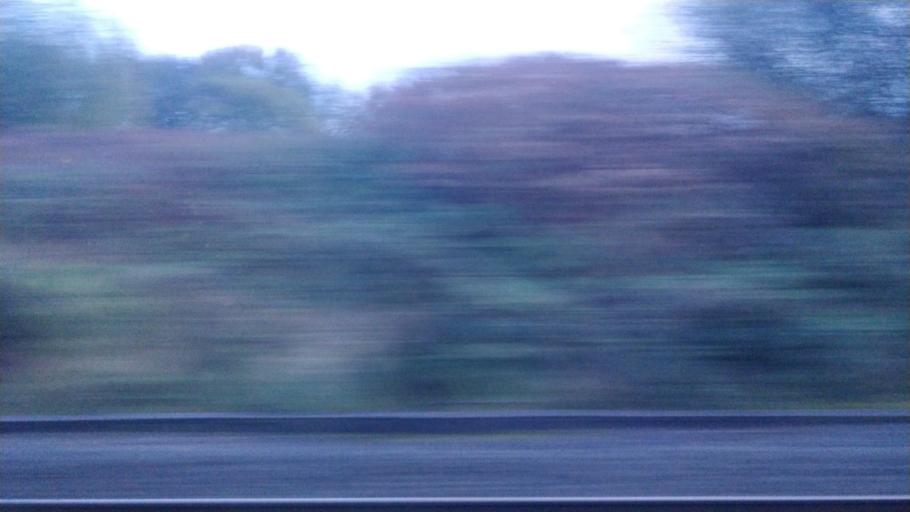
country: GB
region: England
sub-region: Borough of Wigan
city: Hindley
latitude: 53.5436
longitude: -2.5600
